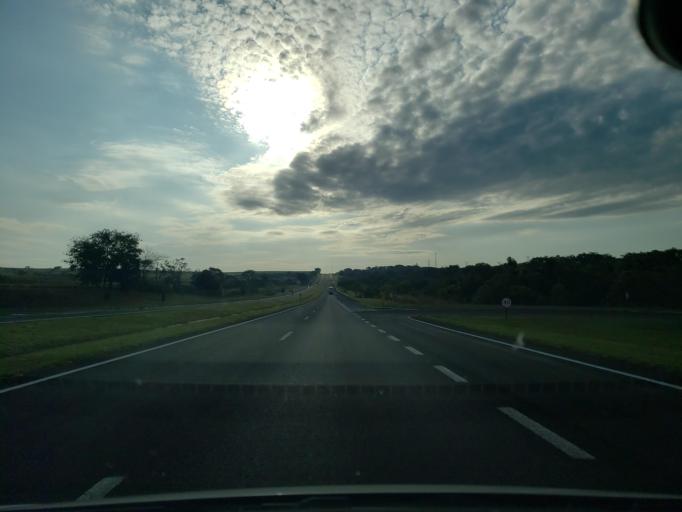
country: BR
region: Sao Paulo
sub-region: Valparaiso
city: Valparaiso
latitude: -21.1680
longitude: -50.9367
